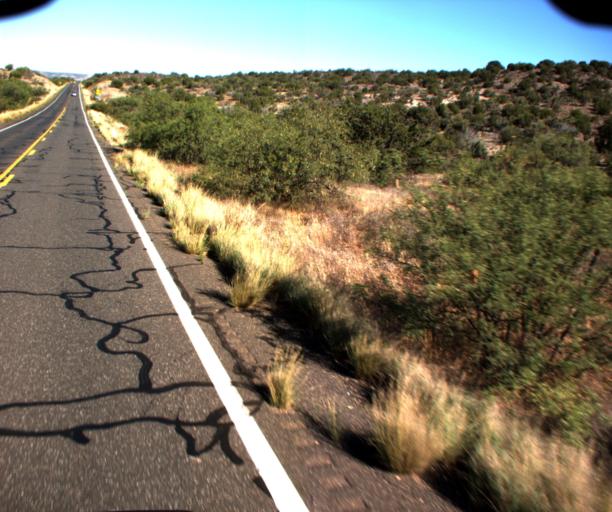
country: US
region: Arizona
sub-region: Yavapai County
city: Lake Montezuma
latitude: 34.6956
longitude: -111.7554
